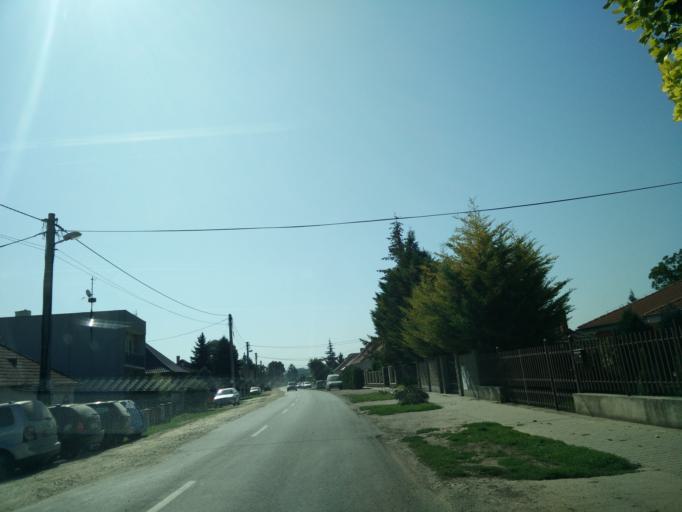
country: SK
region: Nitriansky
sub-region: Okres Nitra
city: Nitra
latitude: 48.3336
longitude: 18.0346
